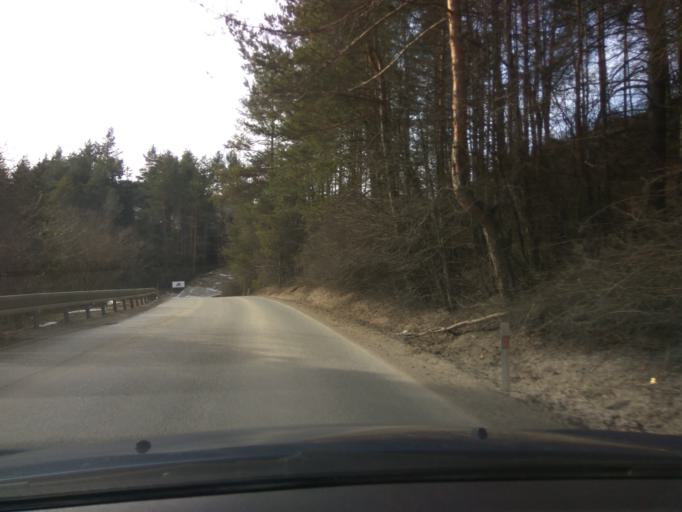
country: SK
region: Zilinsky
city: Rajec
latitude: 49.0885
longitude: 18.6040
